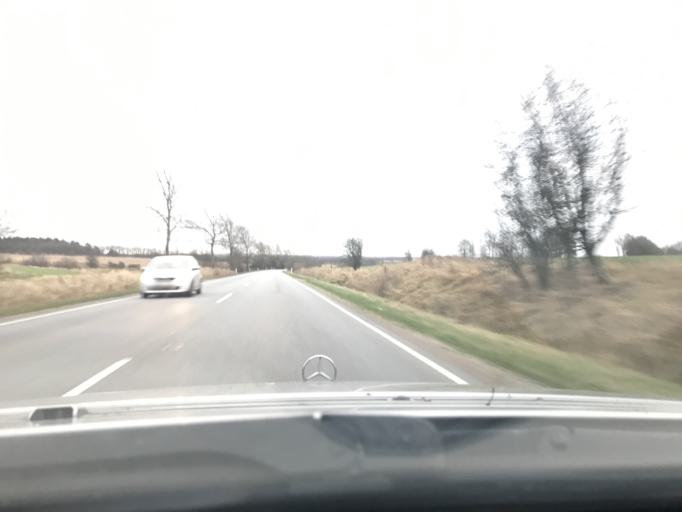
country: DK
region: South Denmark
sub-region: Aabenraa Kommune
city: Rodekro
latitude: 55.0863
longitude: 9.2124
